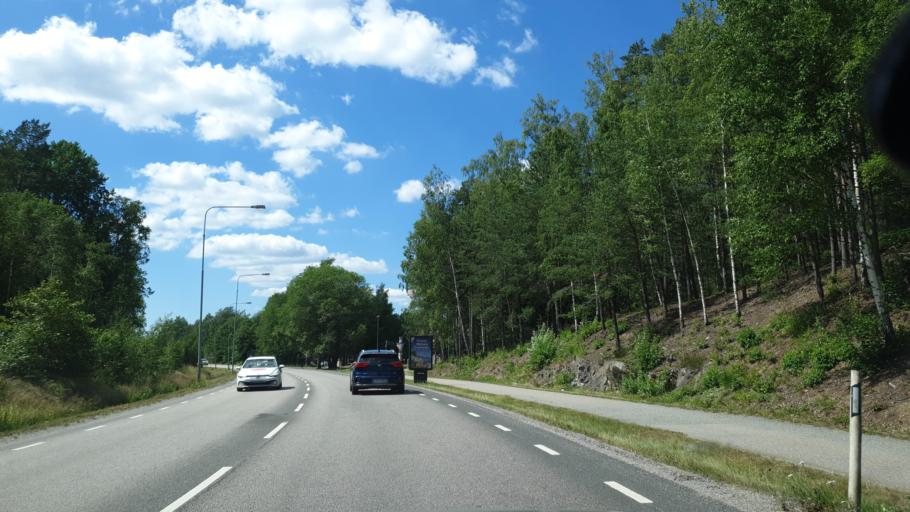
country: SE
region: Stockholm
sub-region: Sodertalje Kommun
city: Soedertaelje
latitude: 59.2102
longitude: 17.5960
